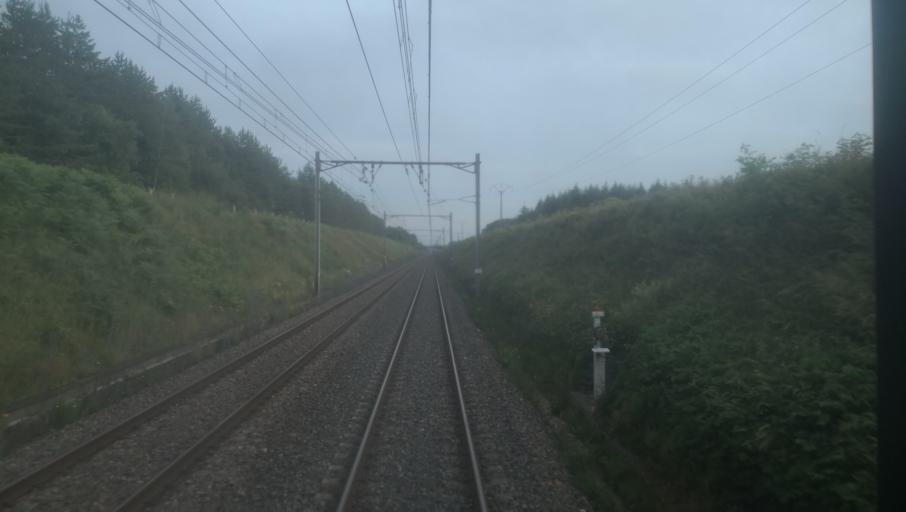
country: FR
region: Centre
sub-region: Departement du Loir-et-Cher
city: Lamotte-Beuvron
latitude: 47.6415
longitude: 1.9904
